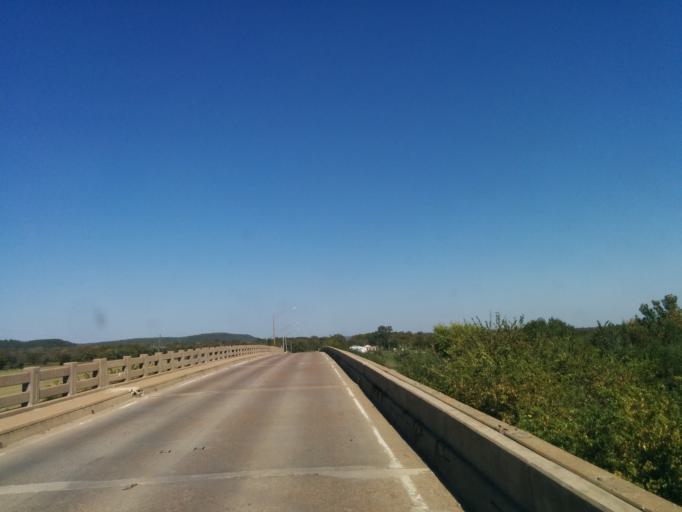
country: US
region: Oklahoma
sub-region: Creek County
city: Mounds
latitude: 35.8818
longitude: -96.0607
